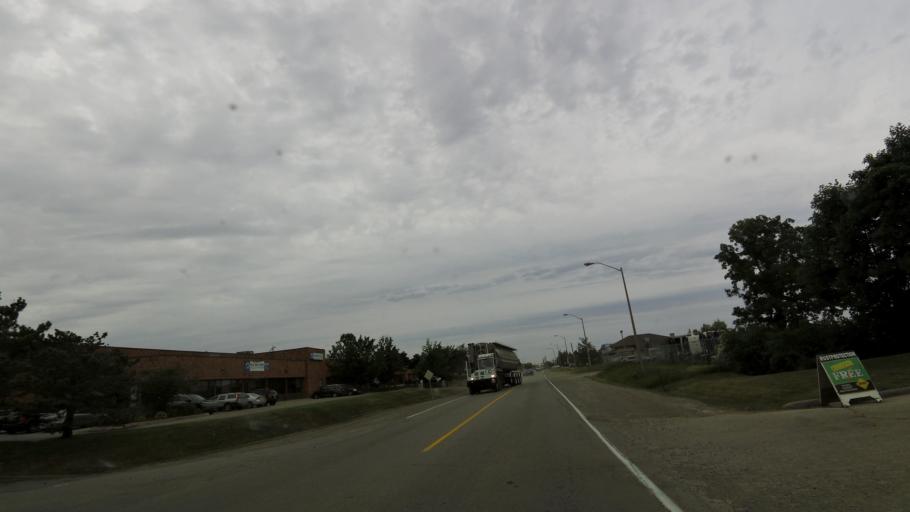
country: CA
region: Ontario
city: Oakville
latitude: 43.4336
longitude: -79.7101
